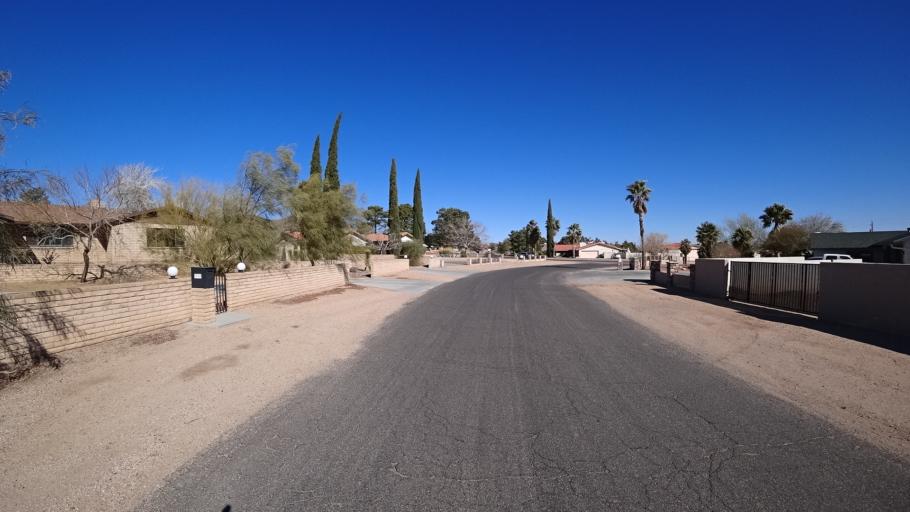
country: US
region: Arizona
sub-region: Mohave County
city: New Kingman-Butler
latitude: 35.2332
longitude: -114.0461
